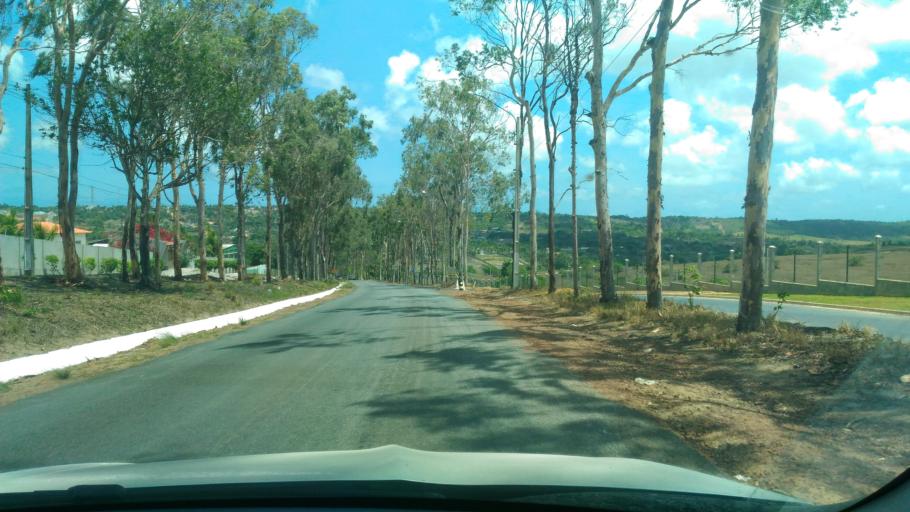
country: BR
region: Paraiba
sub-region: Conde
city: Conde
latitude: -7.2620
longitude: -34.9309
